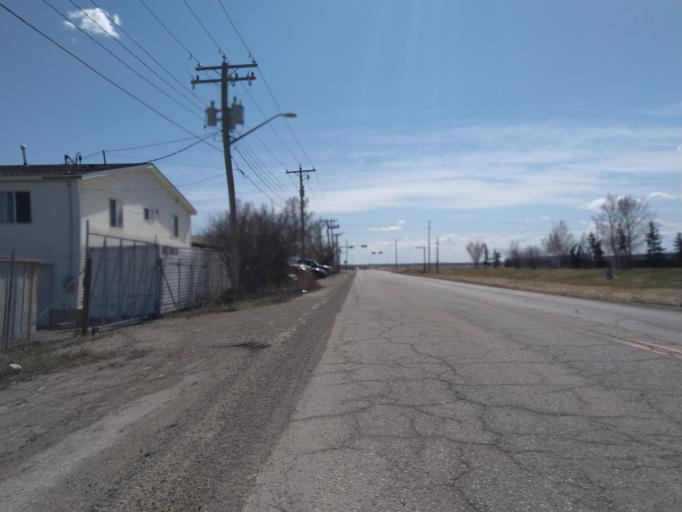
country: CA
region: Alberta
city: Chestermere
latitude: 50.9520
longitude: -113.9120
